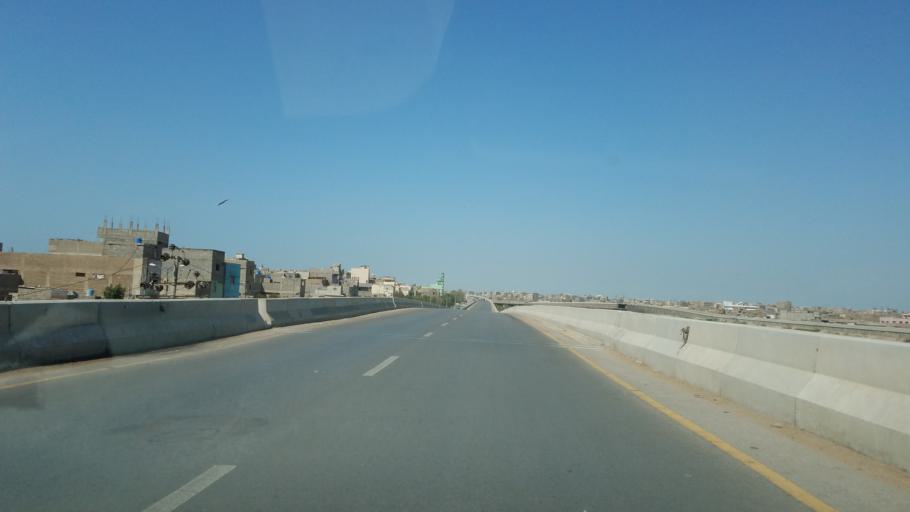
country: PK
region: Sindh
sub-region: Karachi District
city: Karachi
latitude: 24.8807
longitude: 67.0036
